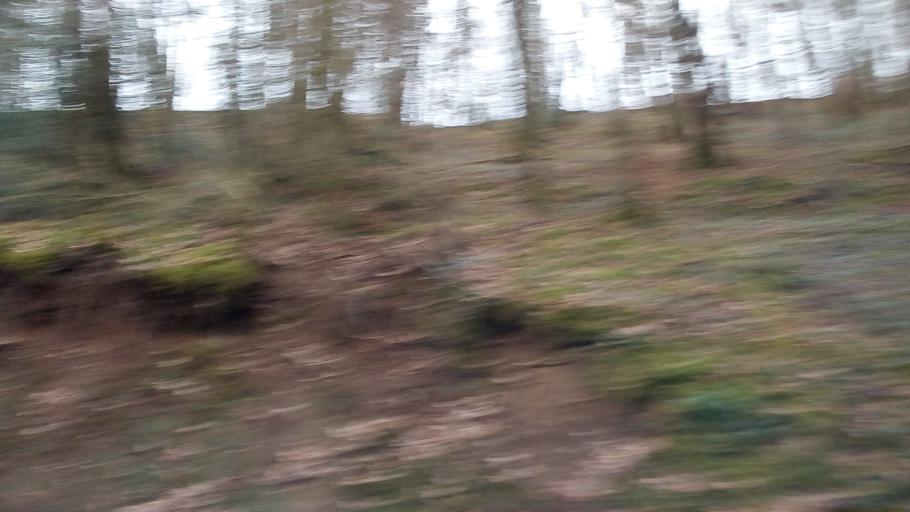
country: FR
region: Limousin
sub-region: Departement de la Correze
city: Naves
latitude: 45.3147
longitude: 1.7770
